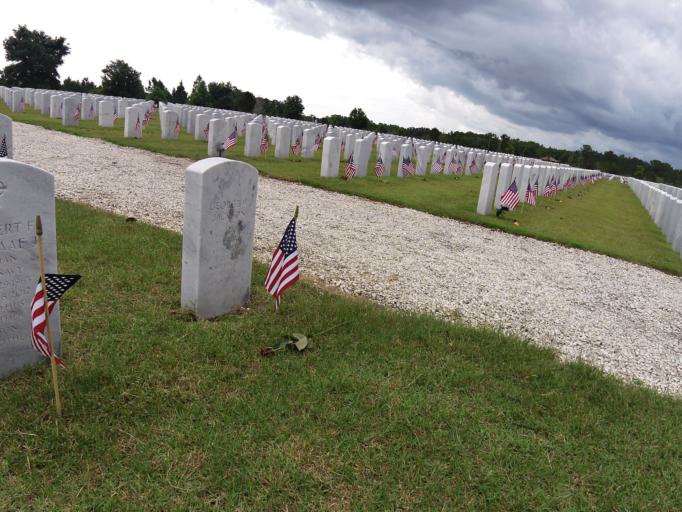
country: US
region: Florida
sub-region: Nassau County
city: Nassau Village-Ratliff
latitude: 30.5455
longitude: -81.7208
